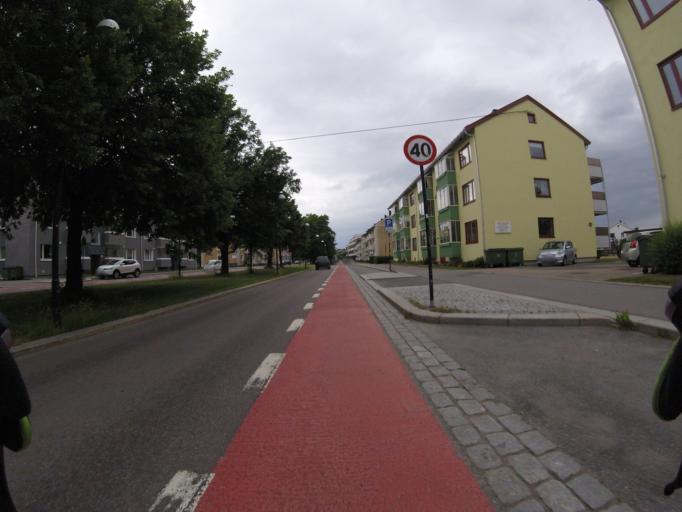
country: NO
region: Akershus
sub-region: Skedsmo
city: Lillestrom
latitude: 59.9595
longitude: 11.0558
